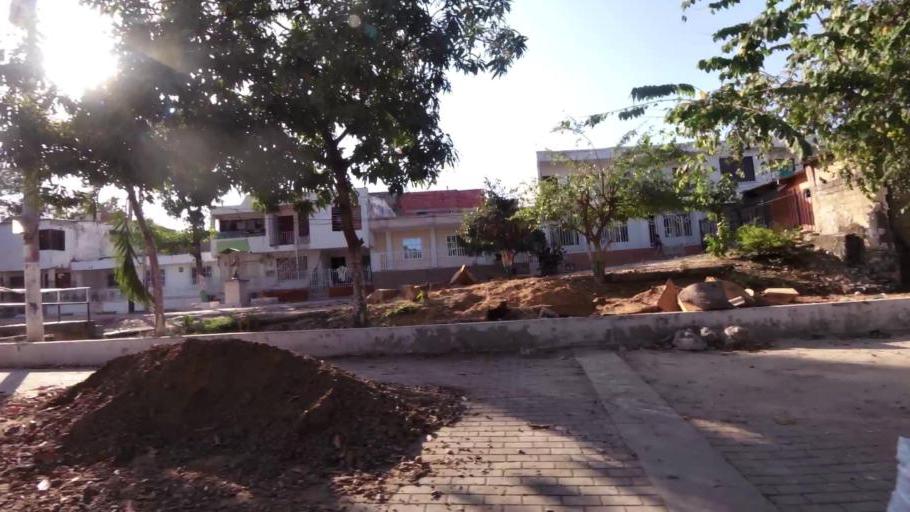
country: CO
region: Bolivar
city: Cartagena
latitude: 10.3803
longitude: -75.4837
